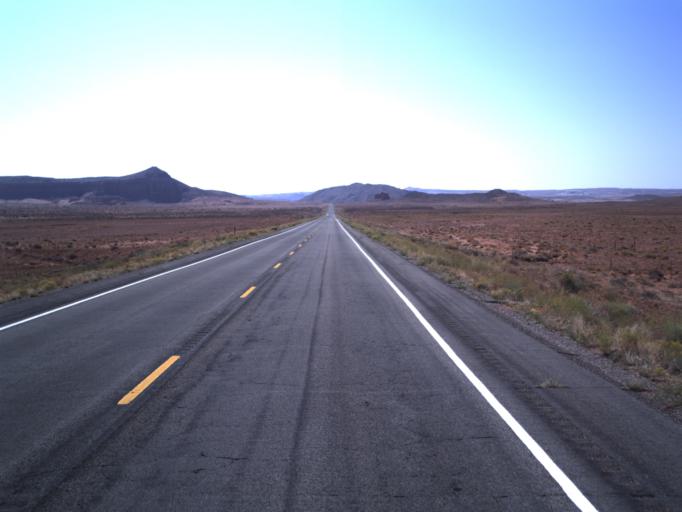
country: US
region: Utah
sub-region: San Juan County
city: Blanding
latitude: 37.0072
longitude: -109.6113
